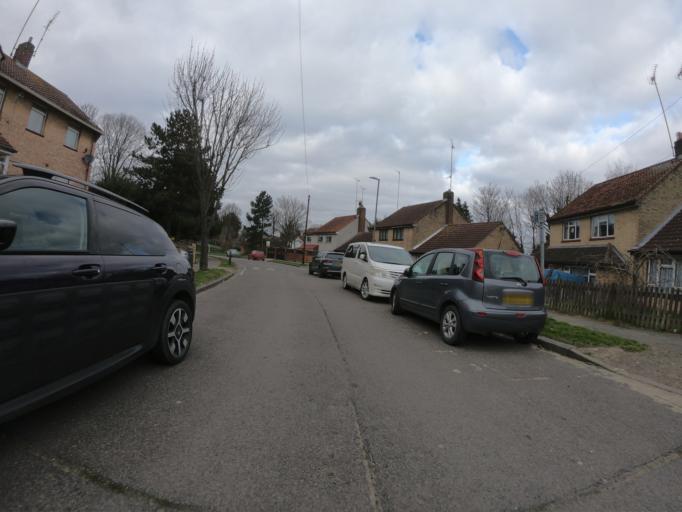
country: GB
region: England
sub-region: Greater London
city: Erith
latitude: 51.4753
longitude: 0.1718
